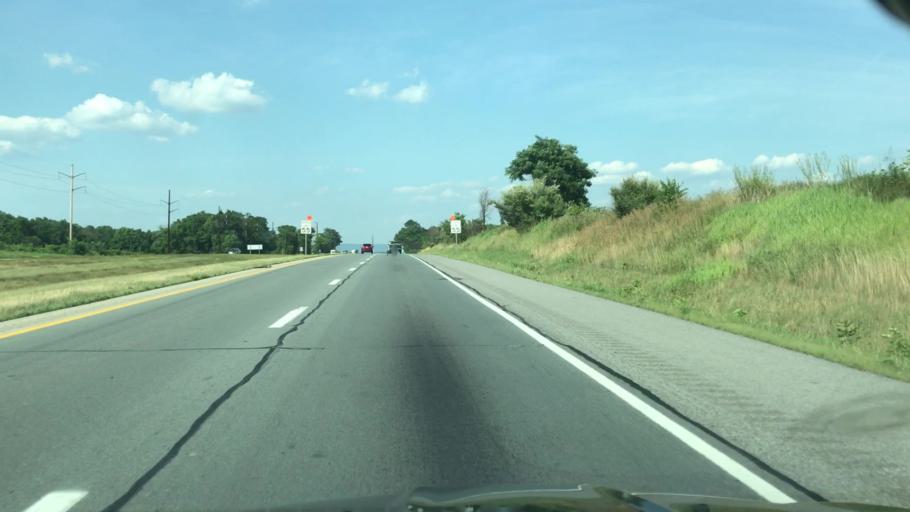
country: US
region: Pennsylvania
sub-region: Cumberland County
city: Carlisle
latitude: 40.1777
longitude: -77.2518
